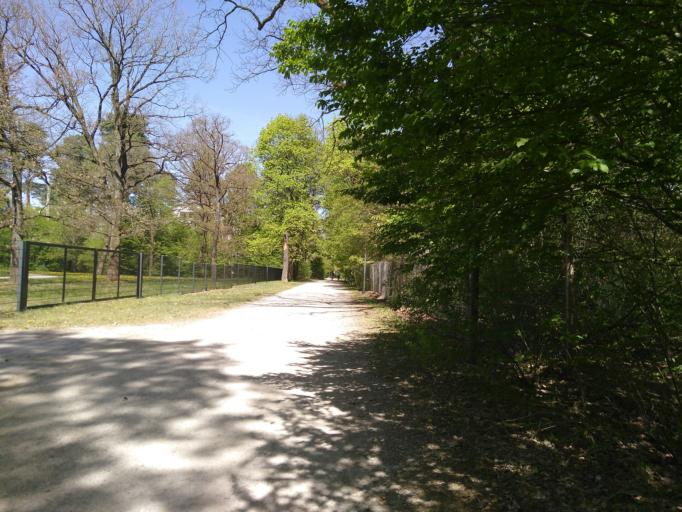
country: DE
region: Bavaria
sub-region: Upper Bavaria
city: Unterhaching
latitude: 48.0951
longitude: 11.6014
